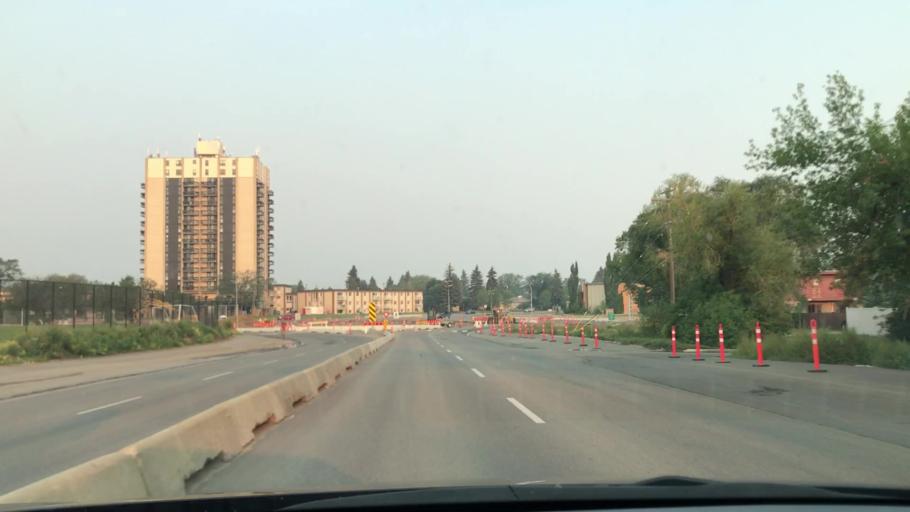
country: CA
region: Alberta
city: Edmonton
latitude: 53.5257
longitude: -113.4555
